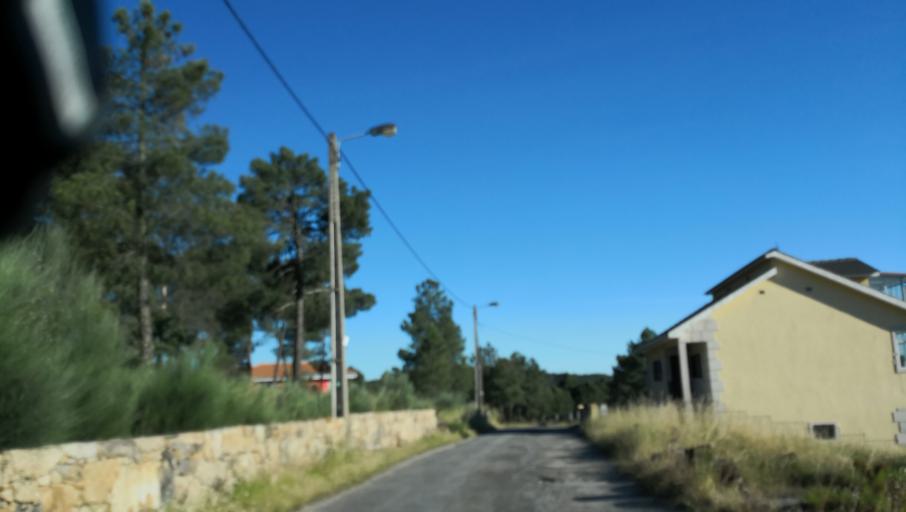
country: PT
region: Vila Real
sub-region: Vila Real
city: Vila Real
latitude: 41.3195
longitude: -7.6766
